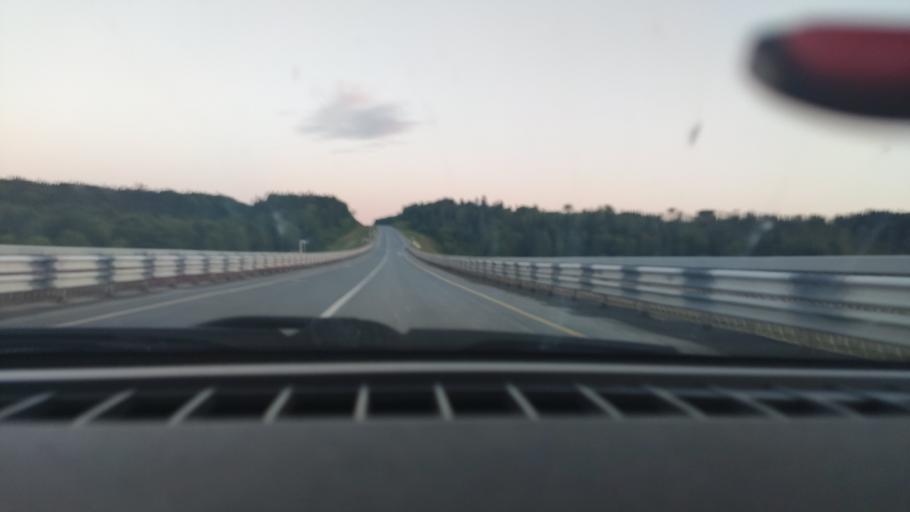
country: RU
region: Perm
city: Polazna
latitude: 58.2834
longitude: 56.4568
